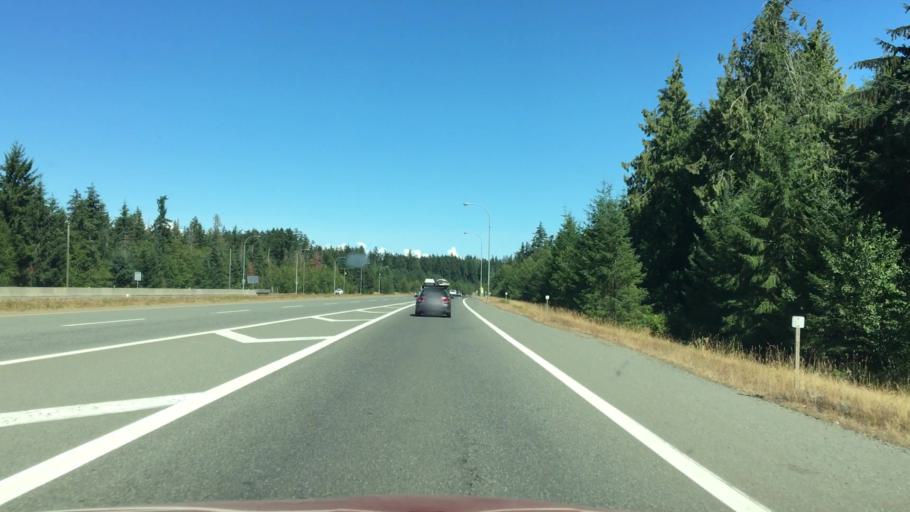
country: CA
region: British Columbia
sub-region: Regional District of Nanaimo
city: Parksville
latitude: 49.3250
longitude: -124.4345
